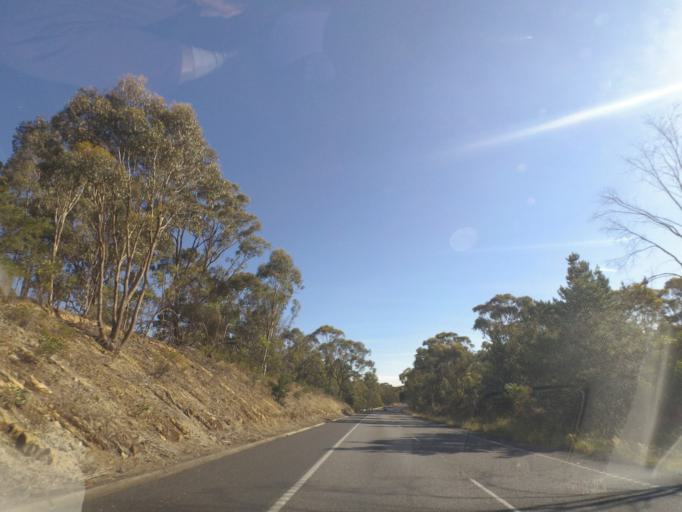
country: AU
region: Victoria
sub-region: Murrindindi
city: Kinglake West
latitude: -37.1717
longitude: 145.0757
